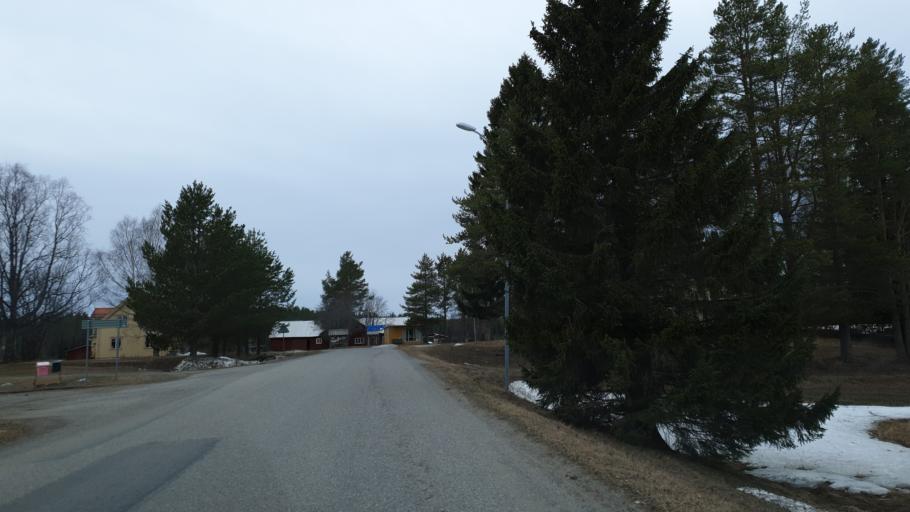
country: SE
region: Vaesterbotten
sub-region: Robertsfors Kommun
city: Robertsfors
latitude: 64.4029
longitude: 21.0102
